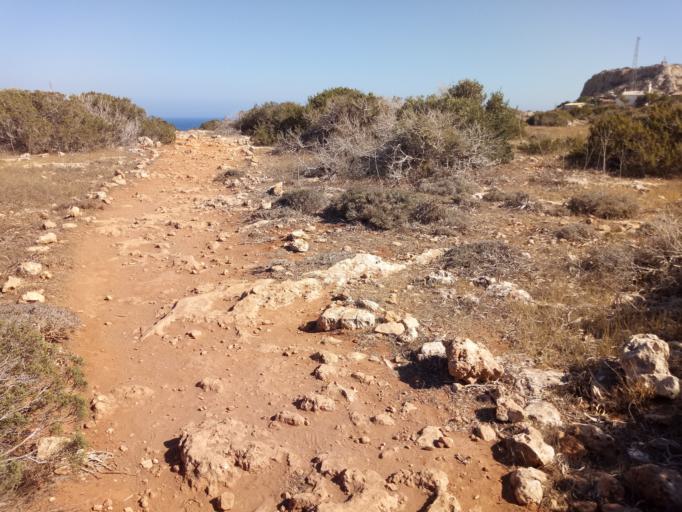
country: CY
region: Ammochostos
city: Protaras
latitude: 34.9694
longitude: 34.0710
